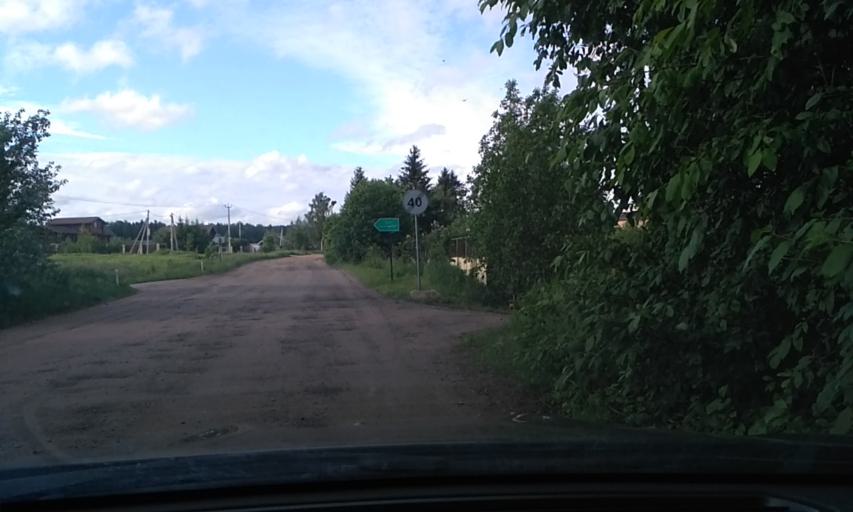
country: RU
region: Leningrad
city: Otradnoye
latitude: 59.7957
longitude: 30.7984
